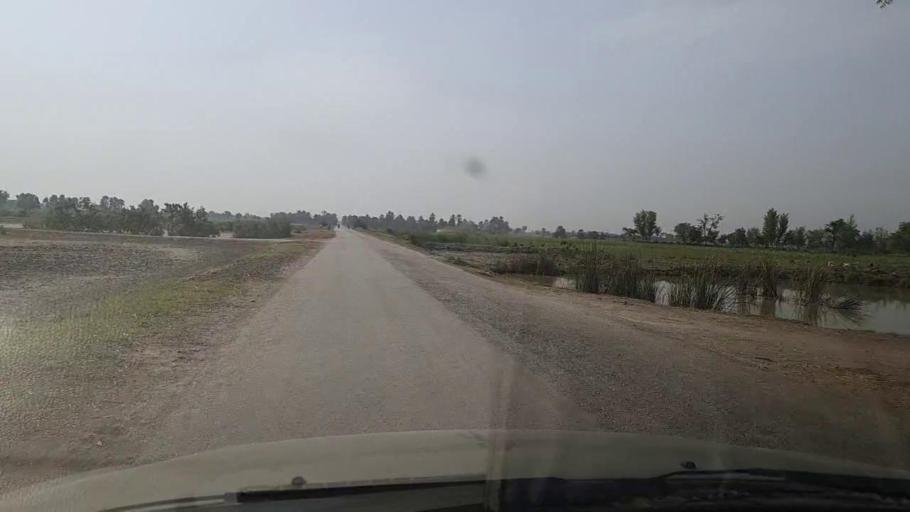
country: PK
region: Sindh
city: Gambat
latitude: 27.4734
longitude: 68.4735
